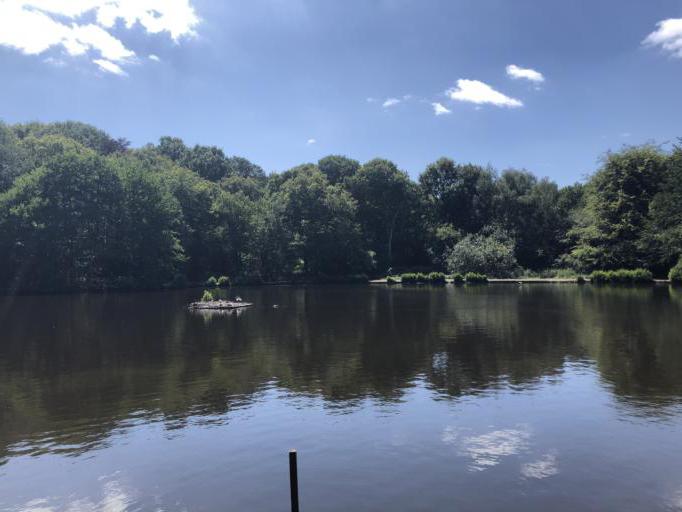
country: GB
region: England
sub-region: Greater London
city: Wandsworth
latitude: 51.4383
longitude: -0.2371
